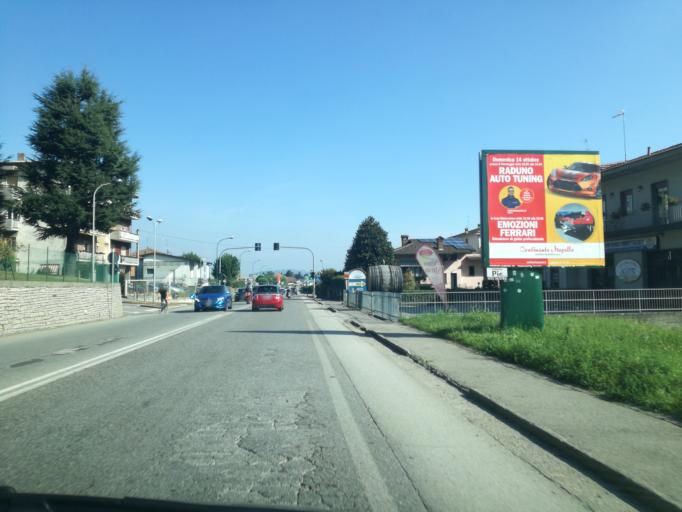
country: IT
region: Lombardy
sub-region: Provincia di Bergamo
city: Pontida
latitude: 45.7311
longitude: 9.5102
